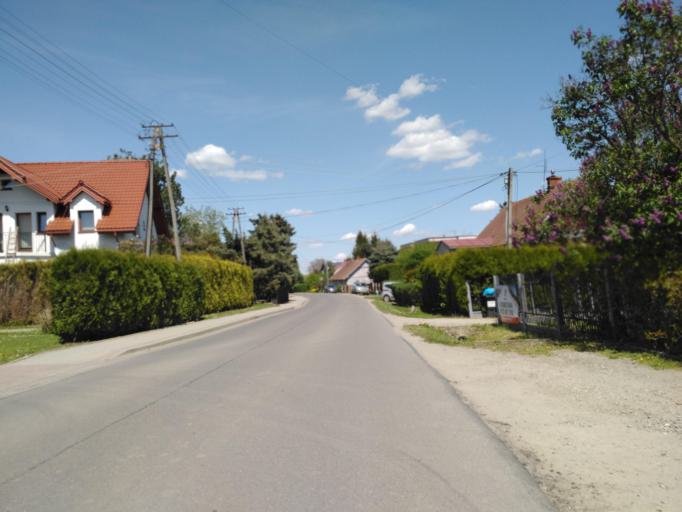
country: PL
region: Subcarpathian Voivodeship
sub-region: Powiat krosnienski
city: Odrzykon
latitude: 49.7140
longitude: 21.7072
